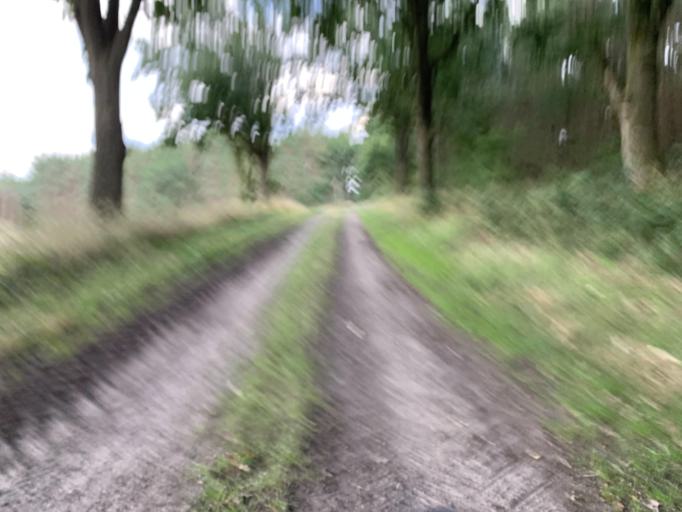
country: DE
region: Lower Saxony
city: Reinstorf
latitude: 53.2147
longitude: 10.5993
